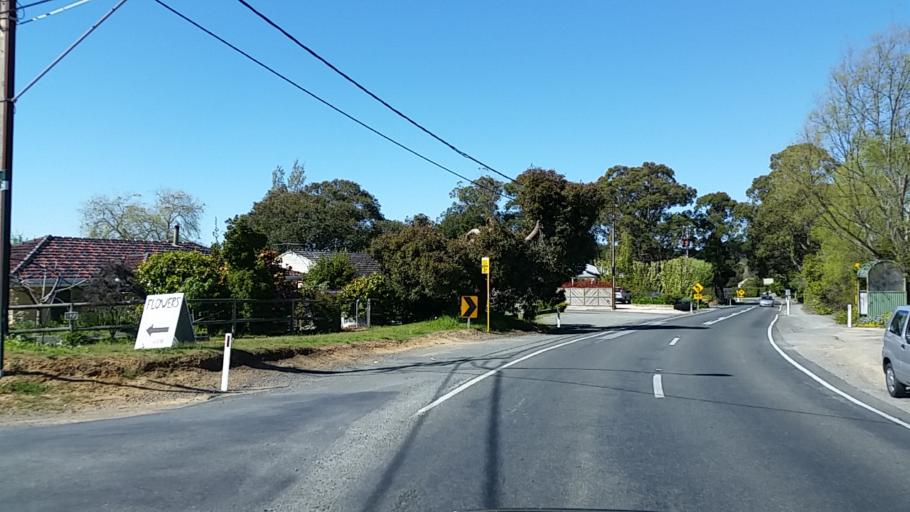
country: AU
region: South Australia
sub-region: Adelaide Hills
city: Bridgewater
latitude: -34.9587
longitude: 138.7367
